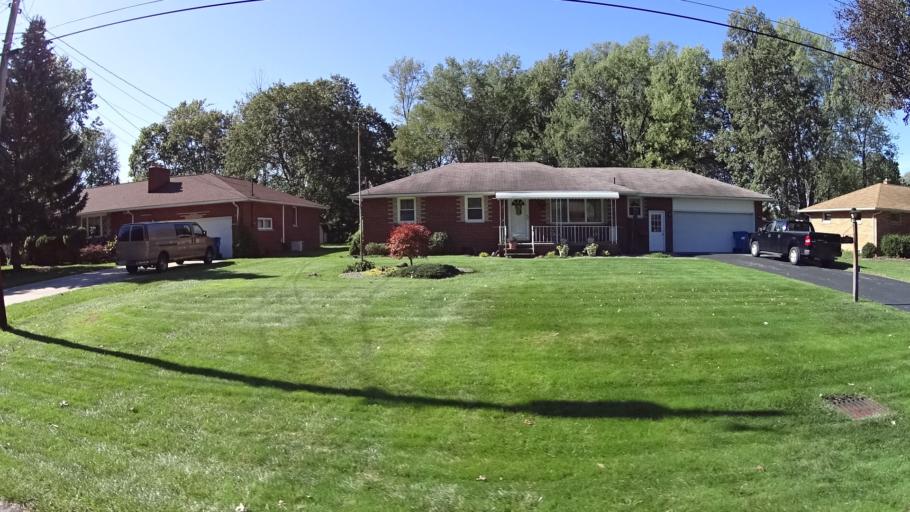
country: US
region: Ohio
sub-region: Lorain County
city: Amherst
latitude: 41.3840
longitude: -82.2191
